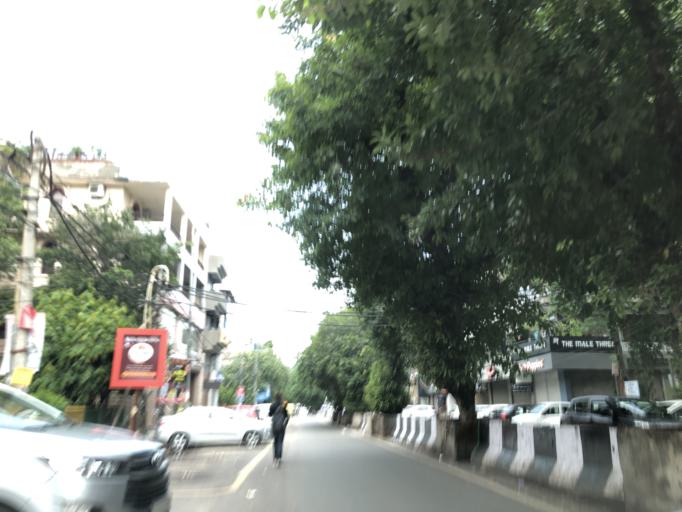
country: IN
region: NCT
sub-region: New Delhi
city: New Delhi
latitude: 28.5702
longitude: 77.2410
